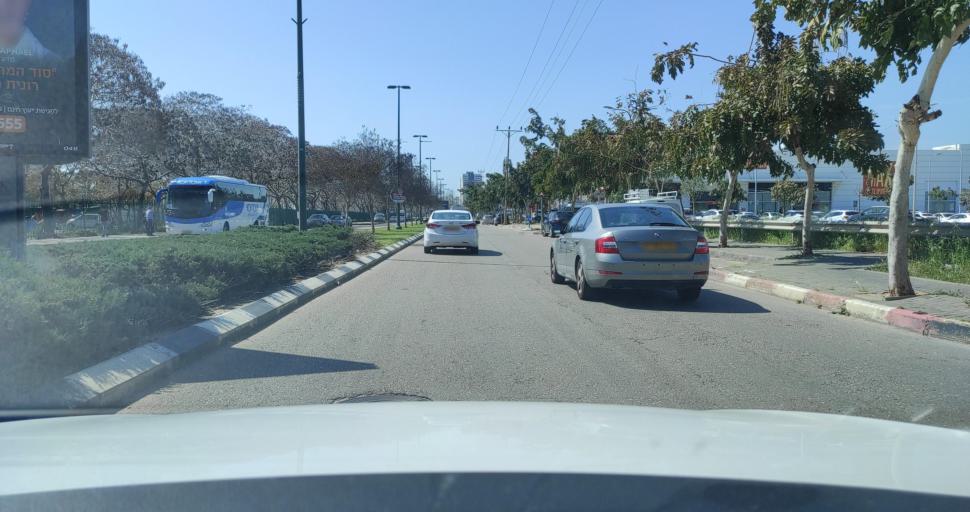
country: IL
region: Central District
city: Nordiyya
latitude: 32.3112
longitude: 34.8755
